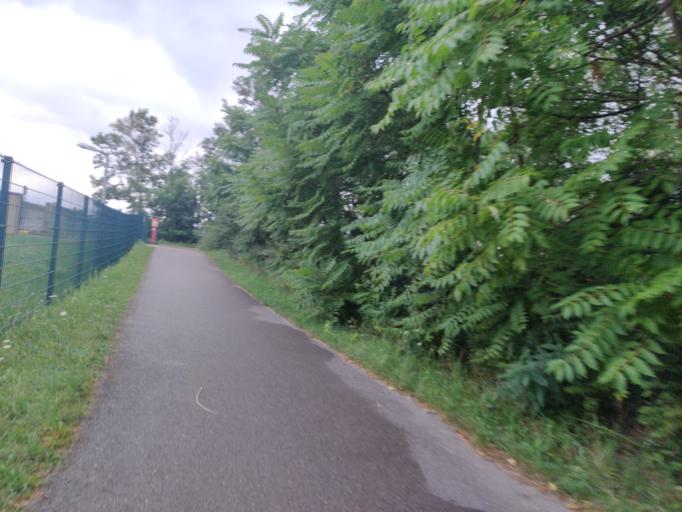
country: AT
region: Lower Austria
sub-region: Politischer Bezirk Korneuburg
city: Spillern
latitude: 48.3514
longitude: 16.2432
